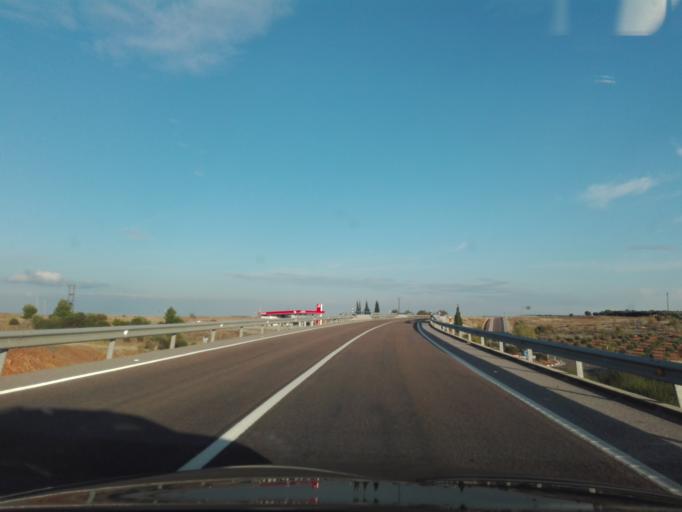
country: ES
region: Extremadura
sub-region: Provincia de Badajoz
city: Usagre
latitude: 38.3450
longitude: -6.1730
